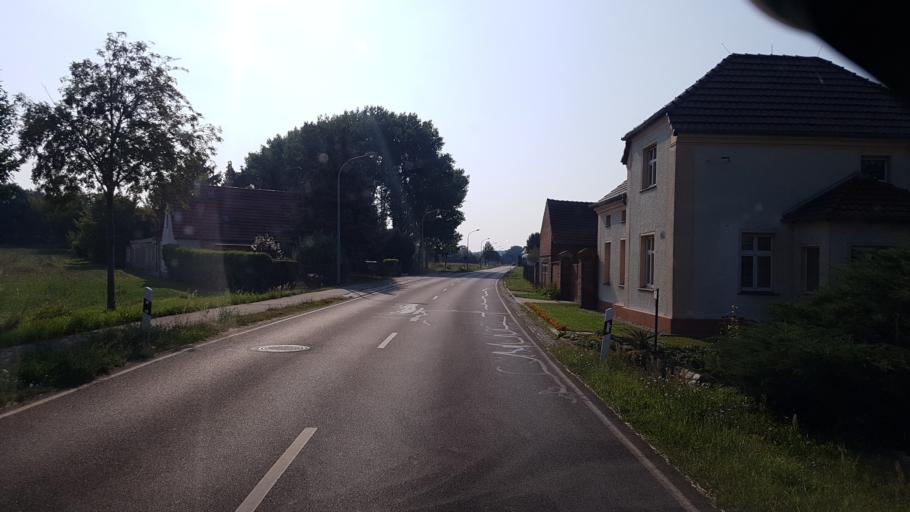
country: DE
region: Brandenburg
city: Drebkau
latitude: 51.6944
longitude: 14.2623
